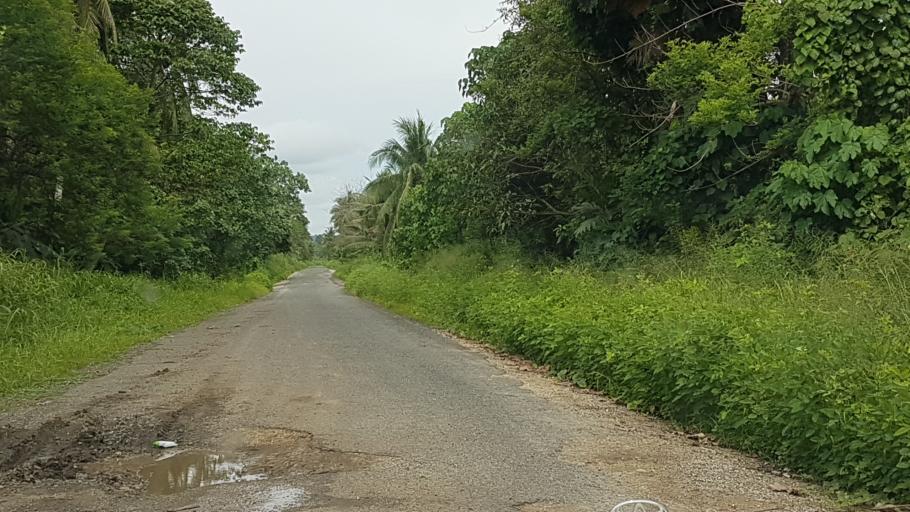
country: PG
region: Madang
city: Madang
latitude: -4.6889
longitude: 145.6044
